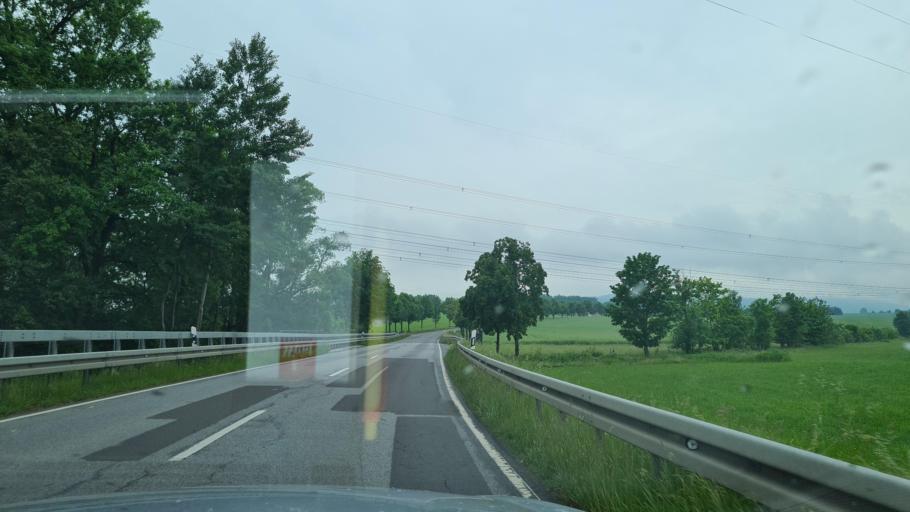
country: DE
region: Saxony
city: Kirschau
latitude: 51.1002
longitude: 14.4434
